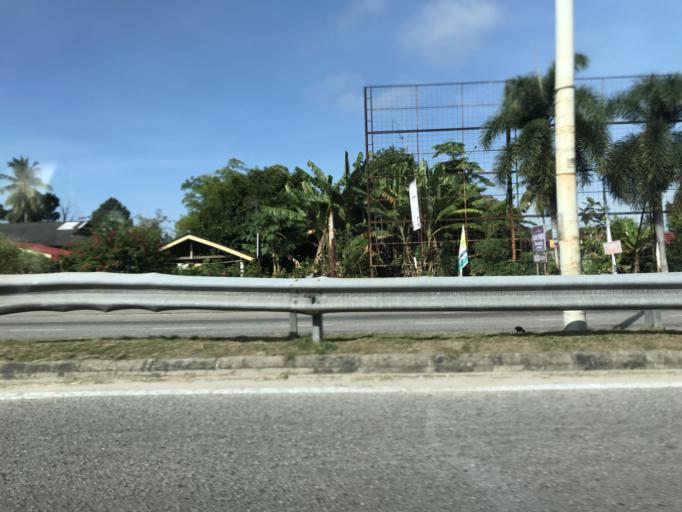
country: MY
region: Kelantan
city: Pasir Mas
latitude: 6.0637
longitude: 102.2053
